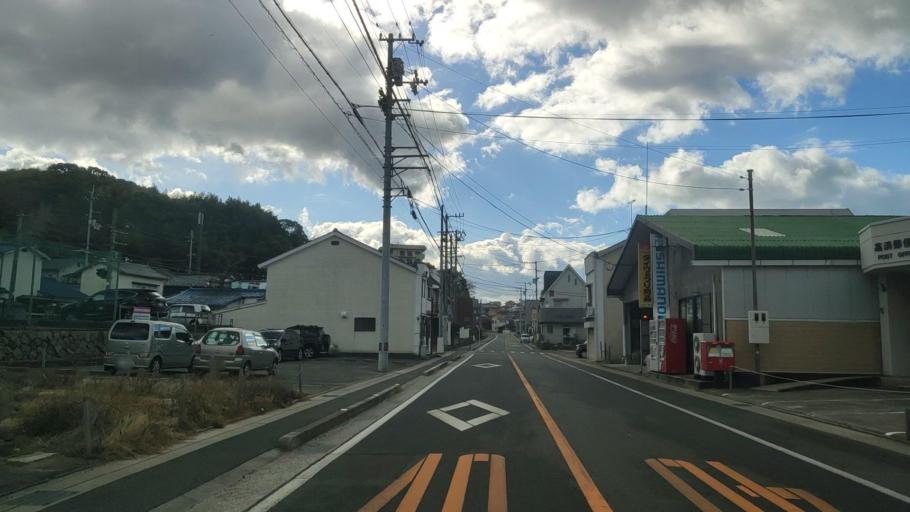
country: JP
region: Ehime
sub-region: Shikoku-chuo Shi
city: Matsuyama
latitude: 33.8831
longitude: 132.7018
